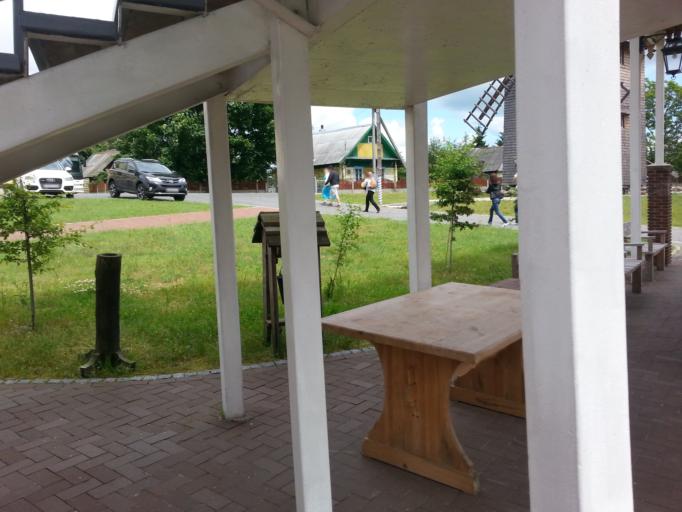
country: BY
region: Minsk
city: Narach
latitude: 54.8617
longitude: 26.7118
